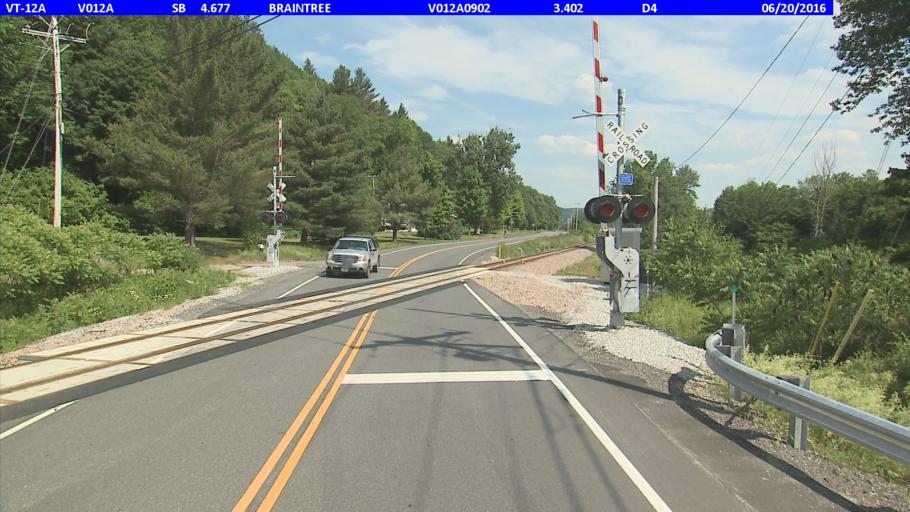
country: US
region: Vermont
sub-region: Orange County
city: Randolph
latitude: 43.9605
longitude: -72.7347
